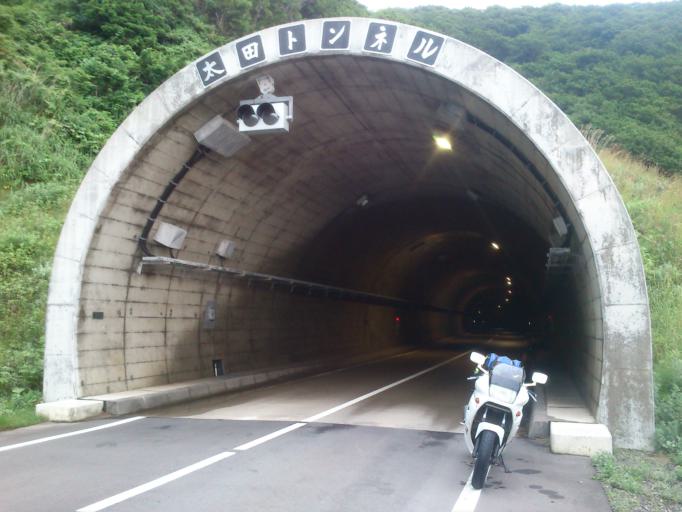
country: JP
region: Hokkaido
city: Iwanai
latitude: 42.3121
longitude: 139.7697
